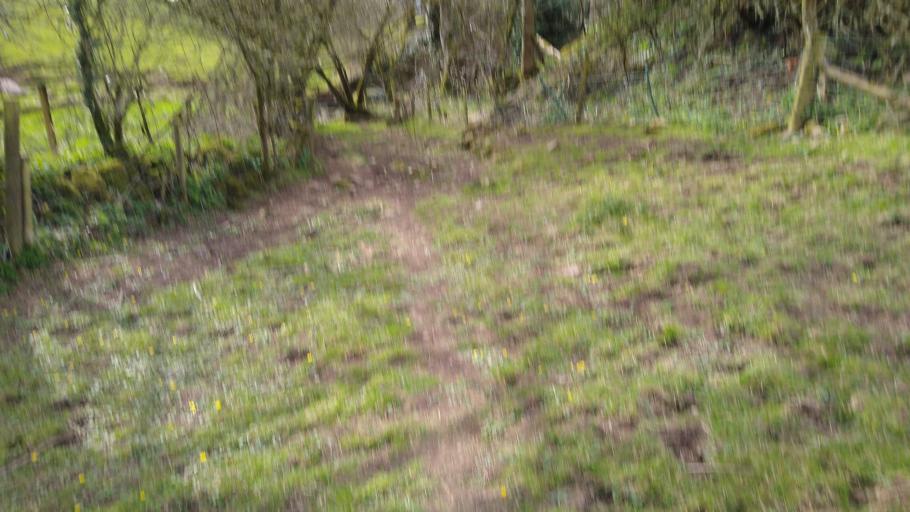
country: GB
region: England
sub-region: Cumbria
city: Cockermouth
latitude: 54.6774
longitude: -3.4059
